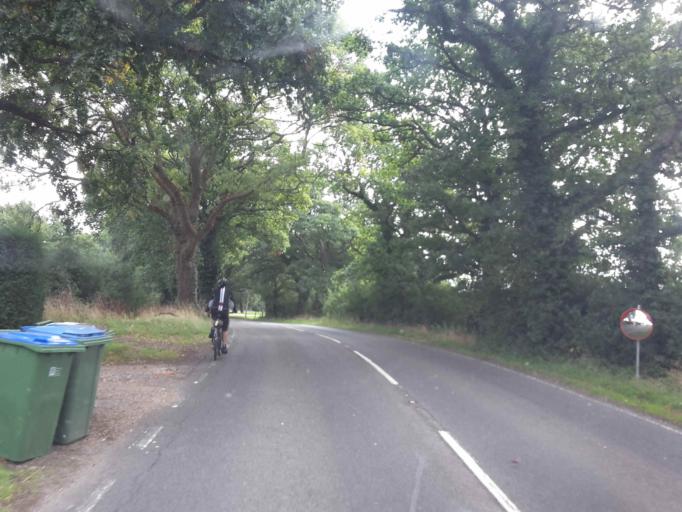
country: GB
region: England
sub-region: West Sussex
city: Ashington
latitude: 50.9476
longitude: -0.3955
